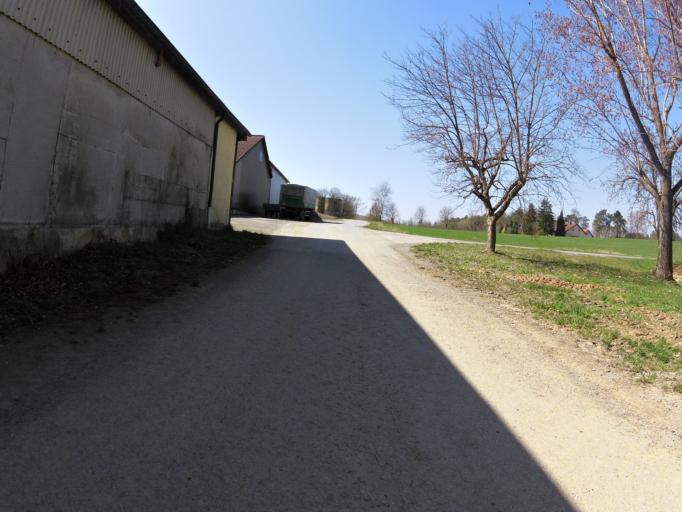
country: DE
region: Bavaria
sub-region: Regierungsbezirk Unterfranken
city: Erlabrunn
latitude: 49.8403
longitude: 9.8302
